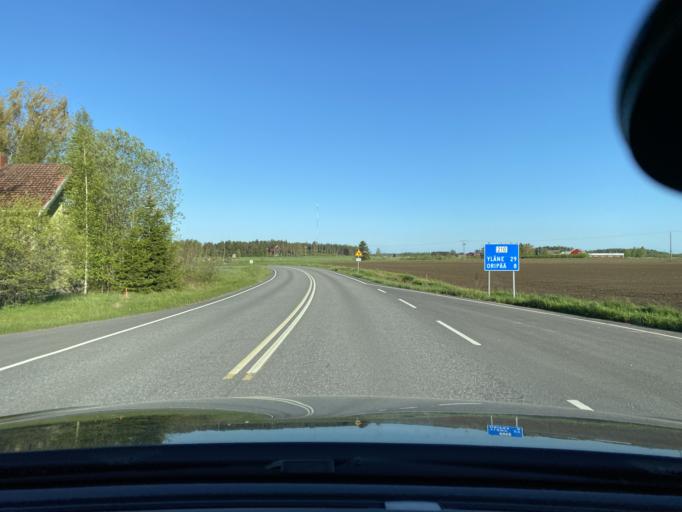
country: FI
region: Varsinais-Suomi
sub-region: Loimaa
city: Alastaro
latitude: 60.8826
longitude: 22.8282
